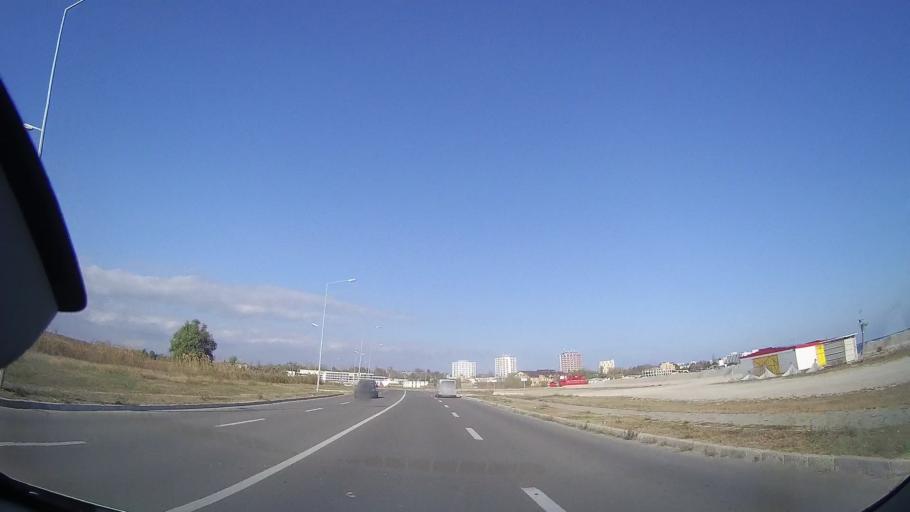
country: RO
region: Constanta
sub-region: Municipiul Mangalia
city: Mangalia
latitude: 43.8390
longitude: 28.5899
